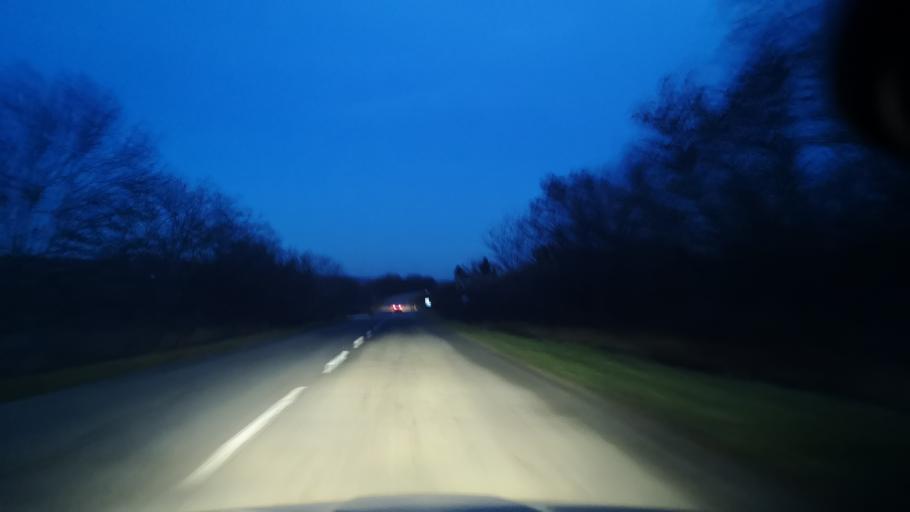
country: MD
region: Orhei
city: Orhei
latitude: 47.3421
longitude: 28.6725
